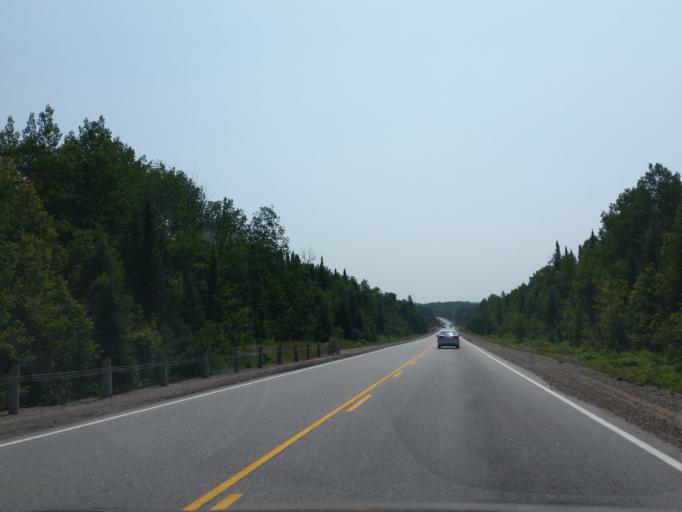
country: CA
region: Ontario
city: Mattawa
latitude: 46.2829
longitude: -78.5032
